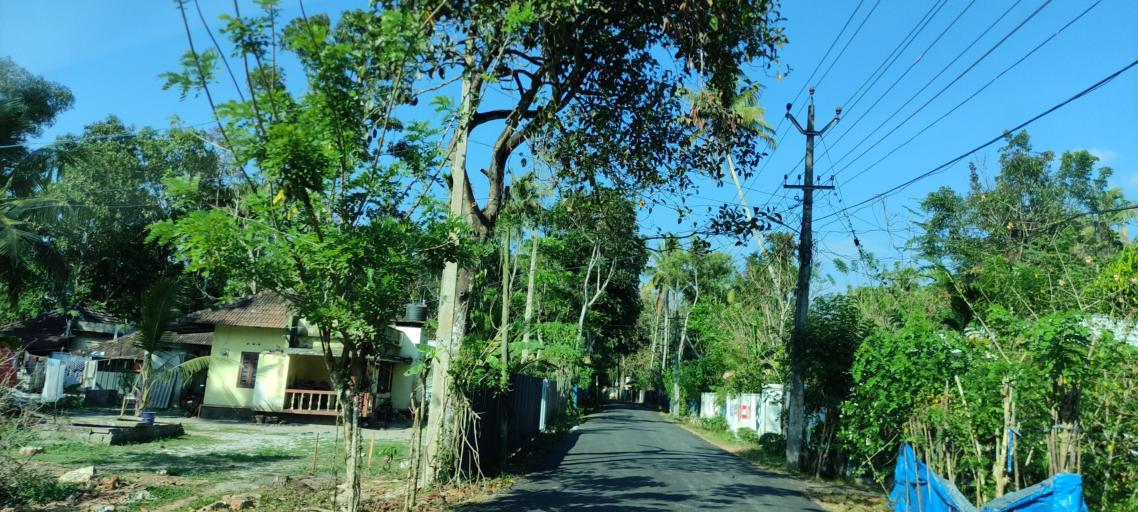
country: IN
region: Kerala
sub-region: Alappuzha
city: Shertallai
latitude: 9.6099
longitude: 76.3398
